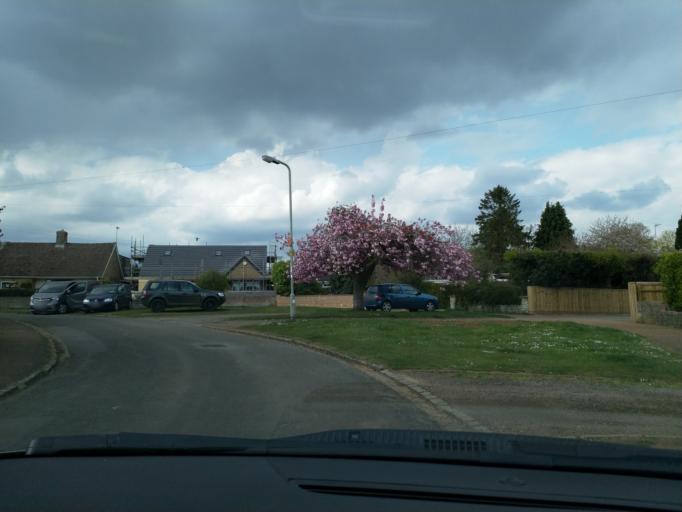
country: GB
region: England
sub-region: Oxfordshire
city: Adderbury
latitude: 52.0237
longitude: -1.3075
